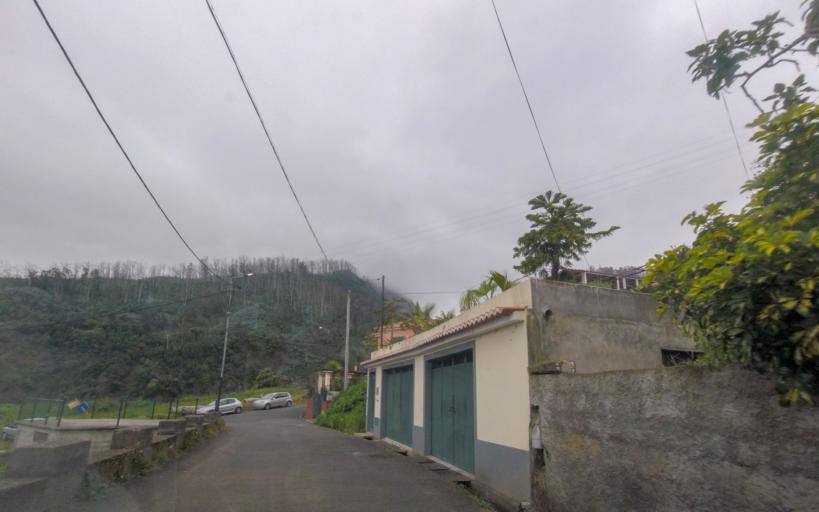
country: PT
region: Madeira
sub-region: Funchal
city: Nossa Senhora do Monte
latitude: 32.6794
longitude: -16.9140
